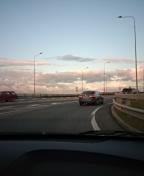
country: RU
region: Moskovskaya
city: Ostrovtsy
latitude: 55.5677
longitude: 38.0388
